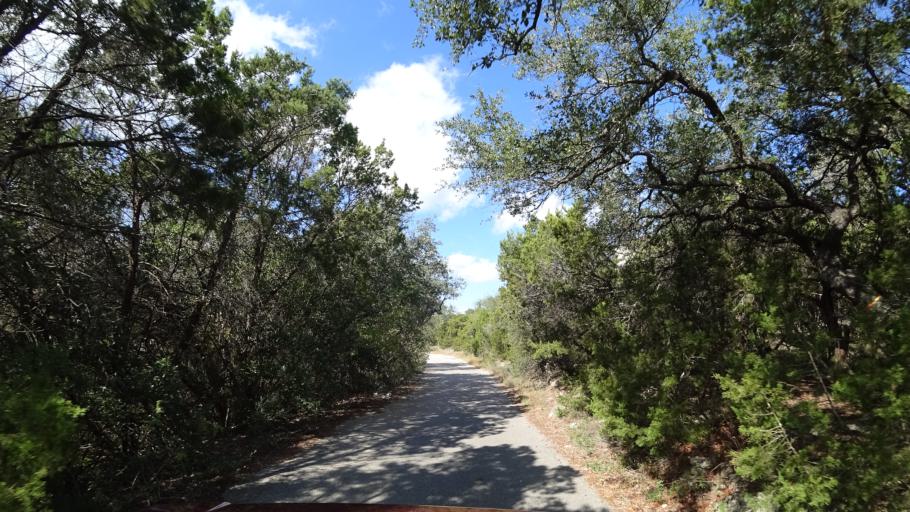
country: US
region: Texas
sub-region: Williamson County
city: Anderson Mill
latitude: 30.4218
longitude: -97.8077
